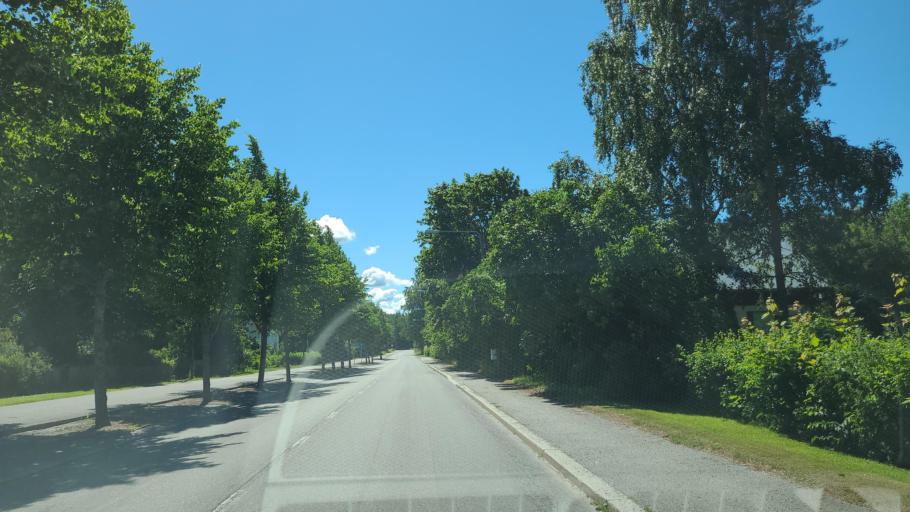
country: FI
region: Ostrobothnia
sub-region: Vaasa
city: Ristinummi
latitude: 63.0718
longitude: 21.7228
